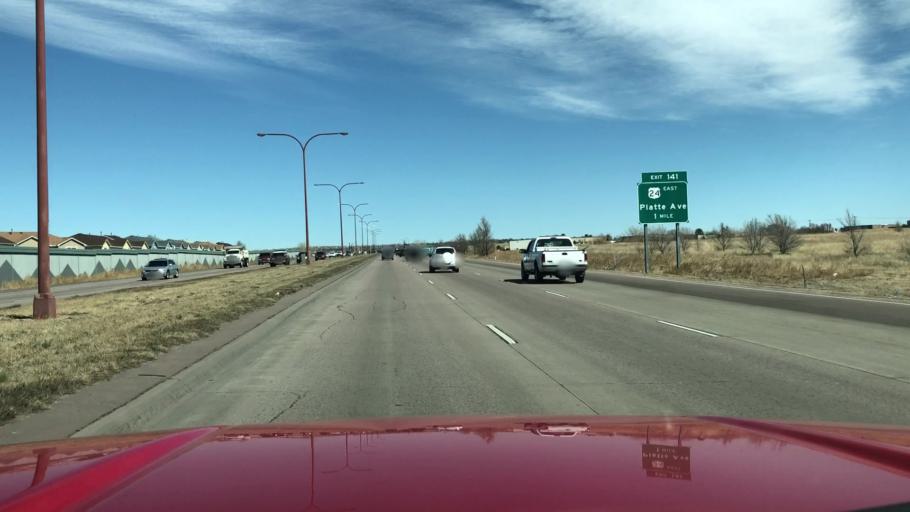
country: US
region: Colorado
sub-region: El Paso County
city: Cimarron Hills
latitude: 38.8186
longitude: -104.7284
